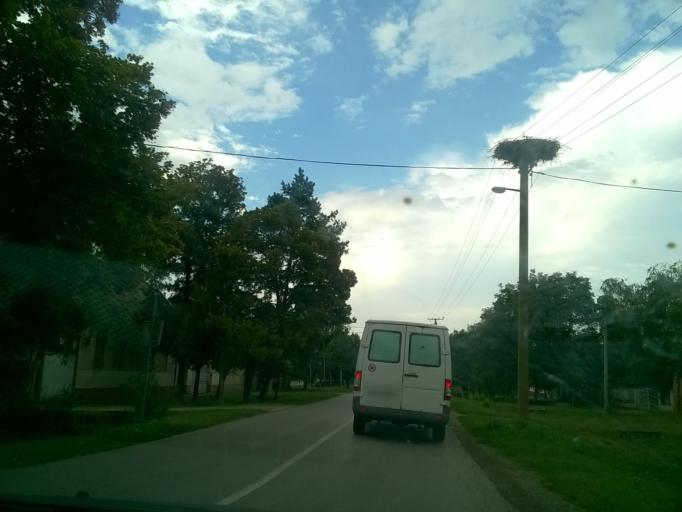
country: RS
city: Tomasevac
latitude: 45.2622
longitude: 20.6178
